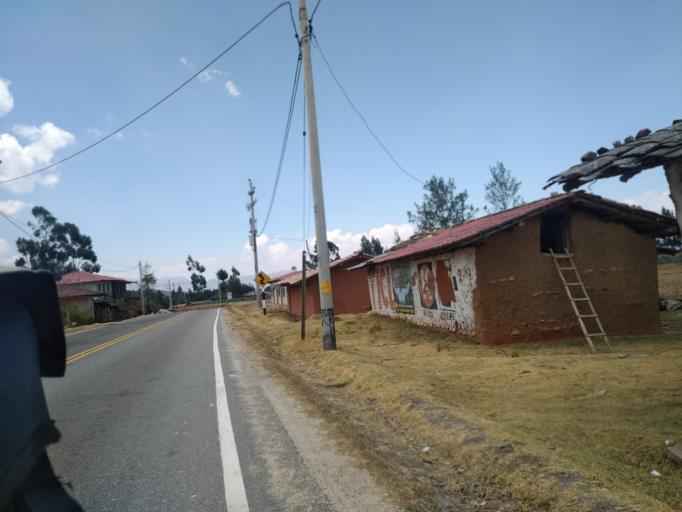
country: PE
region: Cajamarca
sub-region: San Marcos
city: San Marcos
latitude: -7.2821
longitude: -78.2271
